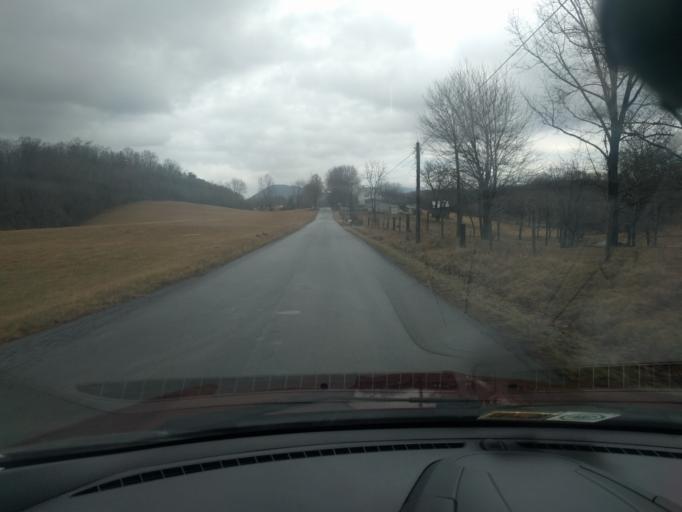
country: US
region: Virginia
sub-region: Botetourt County
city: Fincastle
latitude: 37.5790
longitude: -79.8774
